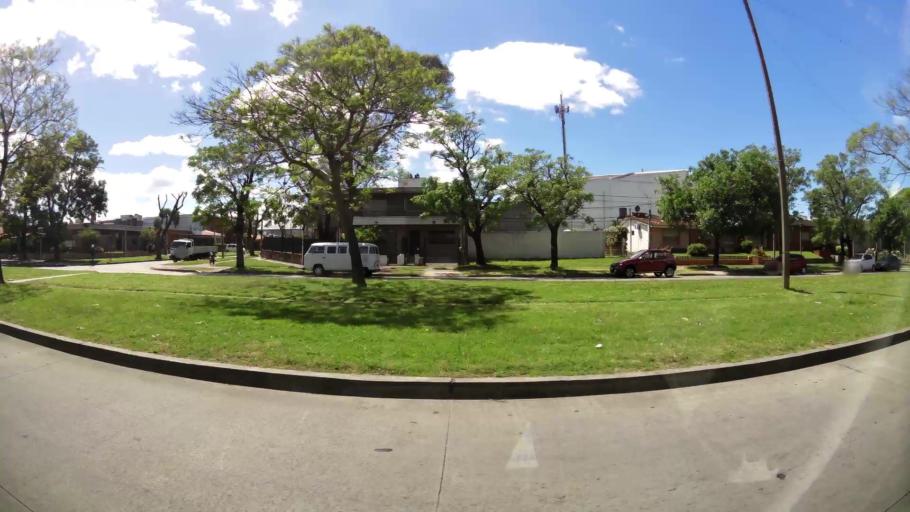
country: UY
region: Montevideo
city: Montevideo
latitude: -34.8609
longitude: -56.1514
